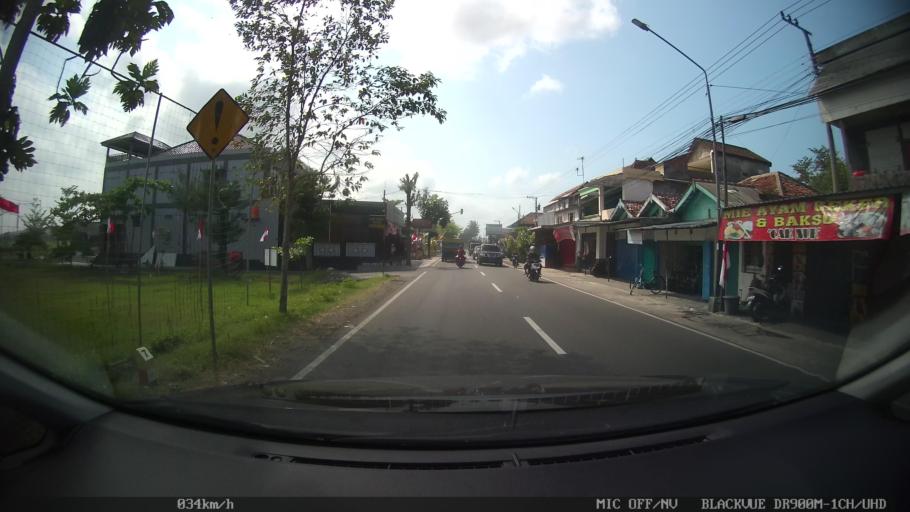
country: ID
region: Daerah Istimewa Yogyakarta
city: Srandakan
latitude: -7.8940
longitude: 110.1448
